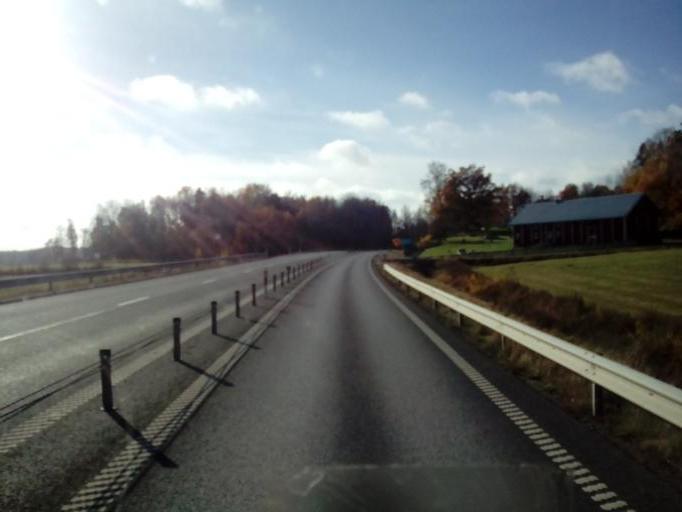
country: SE
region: Kalmar
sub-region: Vimmerby Kommun
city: Vimmerby
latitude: 57.6978
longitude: 16.0153
